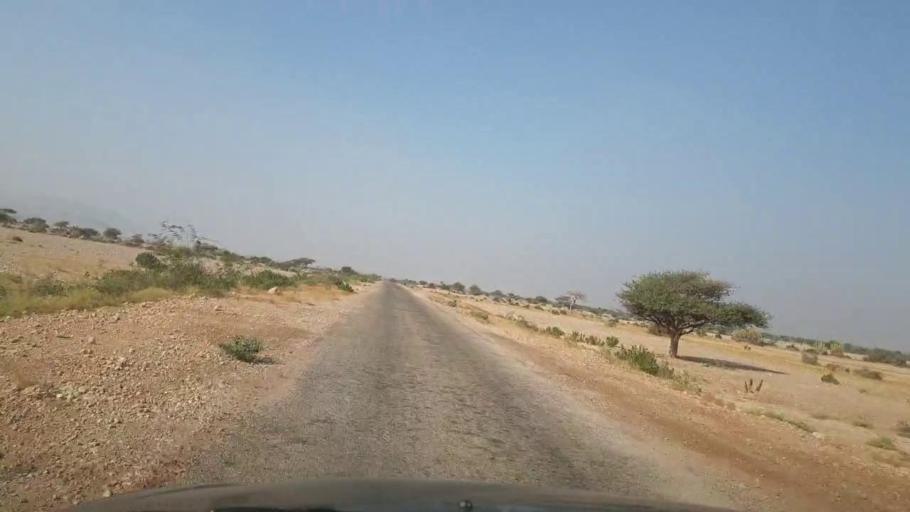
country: PK
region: Sindh
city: Jamshoro
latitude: 25.5794
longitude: 67.8217
